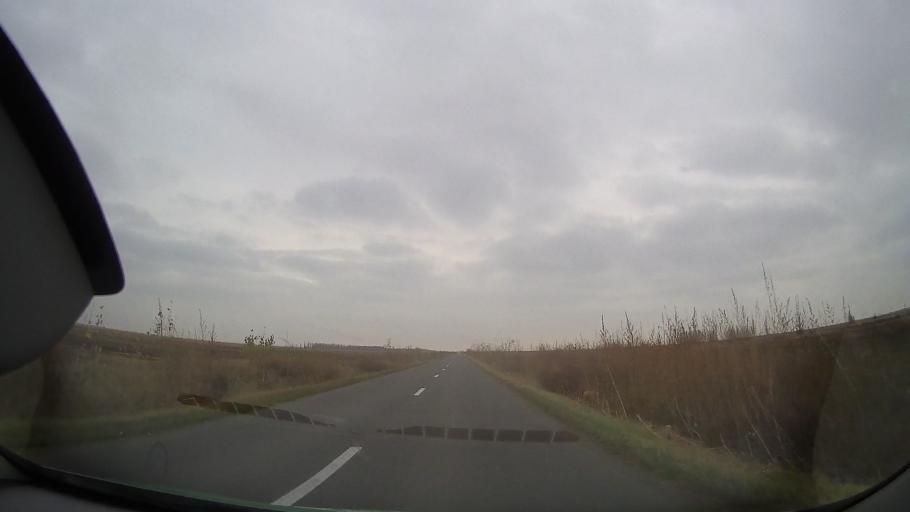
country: RO
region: Ialomita
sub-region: Comuna Garbovi
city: Garbovi
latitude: 44.7491
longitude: 26.7189
